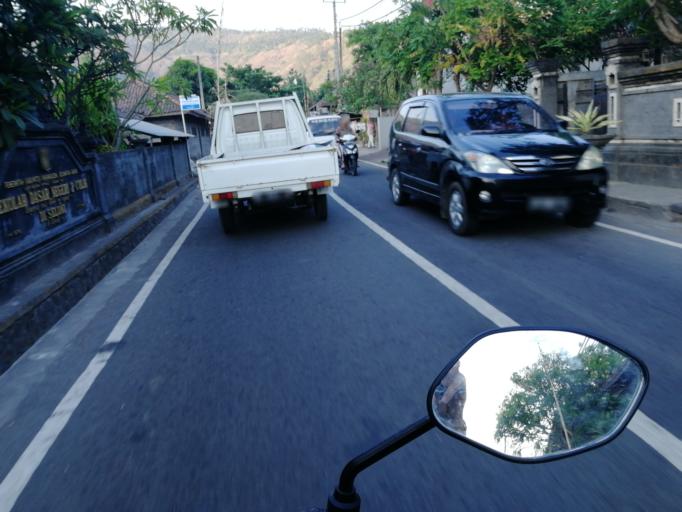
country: ID
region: Bali
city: Banjar Buayang
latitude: -8.3438
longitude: 115.6164
